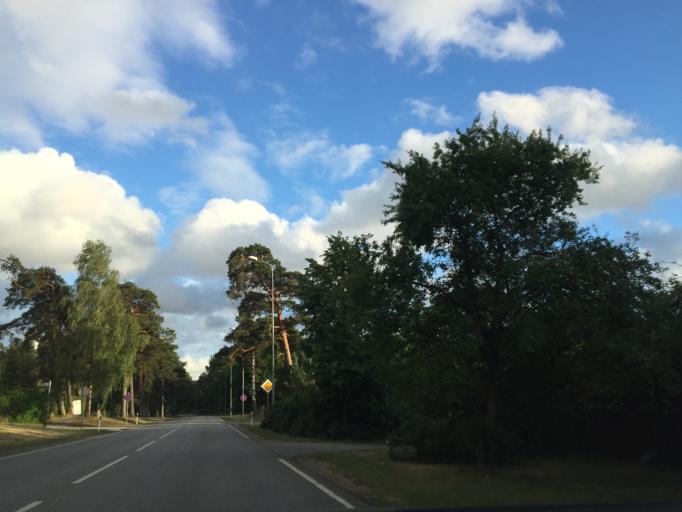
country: LV
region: Saulkrastu
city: Saulkrasti
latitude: 57.2975
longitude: 24.4098
